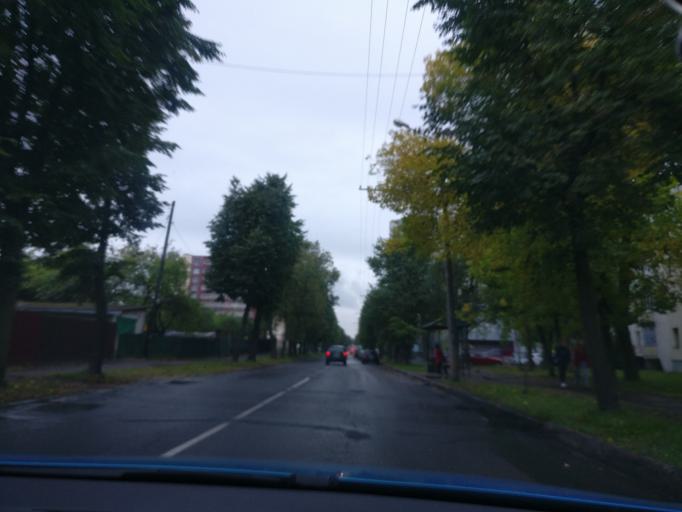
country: BY
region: Minsk
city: Minsk
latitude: 53.9266
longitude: 27.5497
